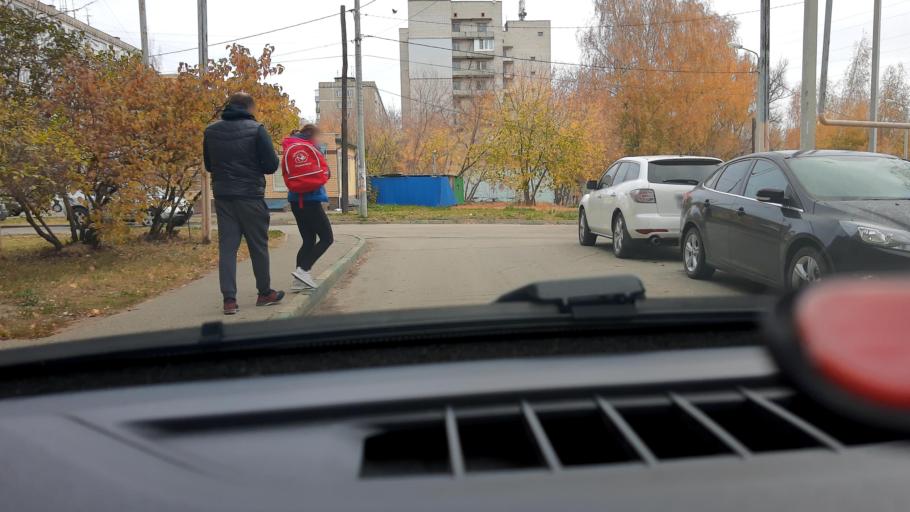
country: RU
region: Nizjnij Novgorod
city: Gorbatovka
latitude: 56.3784
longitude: 43.7971
